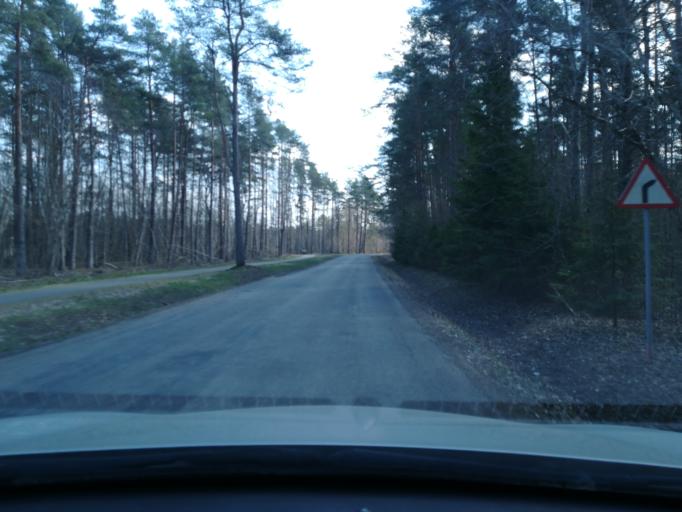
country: EE
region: Harju
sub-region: Saue vald
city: Laagri
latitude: 59.3546
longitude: 24.5843
